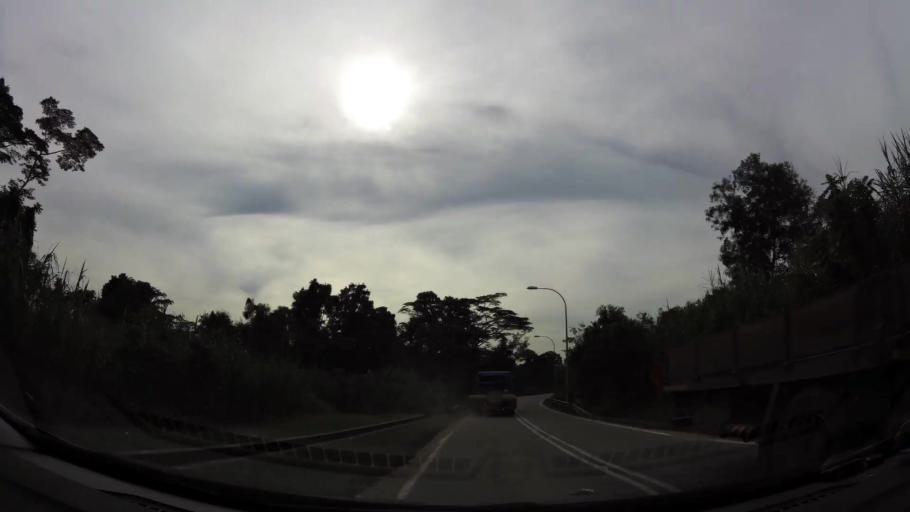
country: MY
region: Johor
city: Johor Bahru
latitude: 1.4164
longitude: 103.7161
